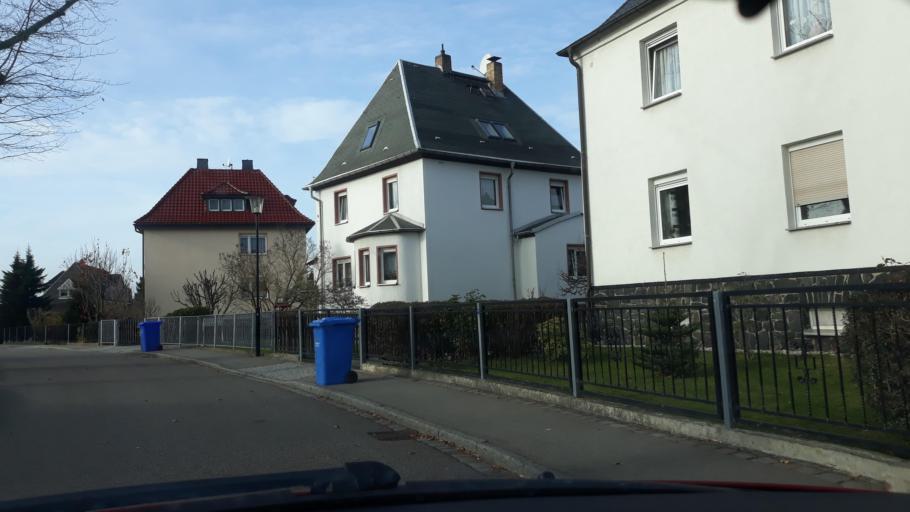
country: DE
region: Saxony
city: Wilkau-Hasslau
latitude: 50.6923
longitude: 12.5404
